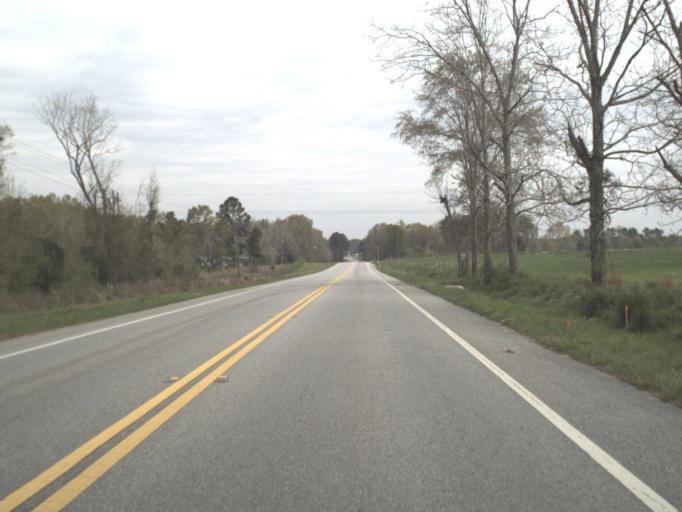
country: US
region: Florida
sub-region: Jackson County
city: Graceville
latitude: 30.9546
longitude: -85.6484
